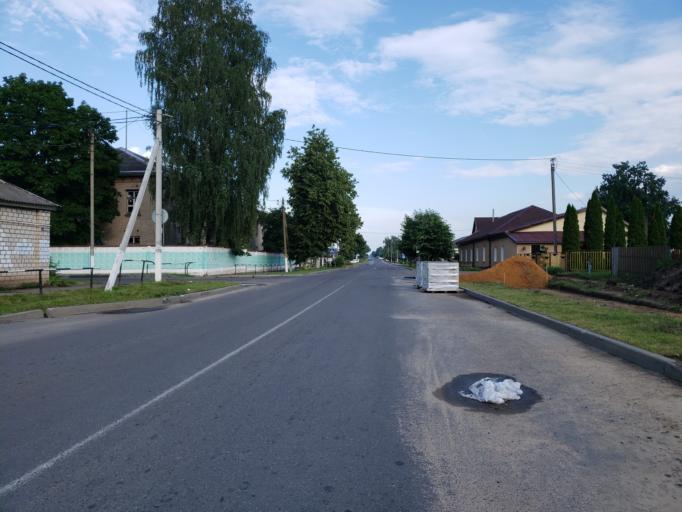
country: BY
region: Minsk
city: Chervyen'
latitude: 53.7086
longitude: 28.4292
